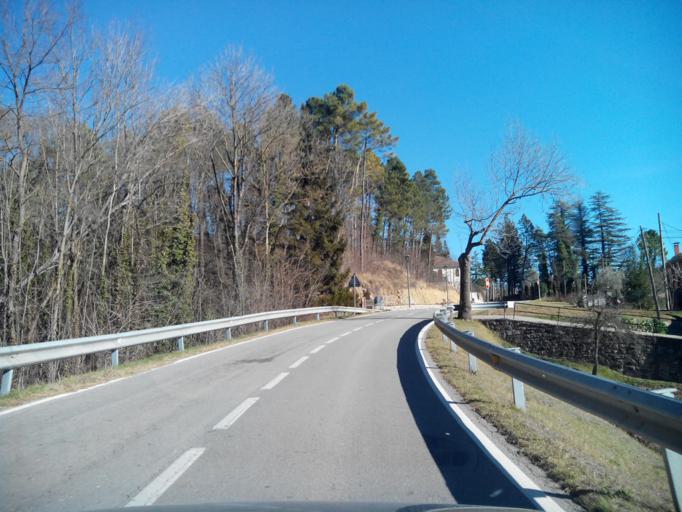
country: ES
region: Catalonia
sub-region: Provincia de Barcelona
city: Vilada
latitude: 42.1358
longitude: 1.9258
